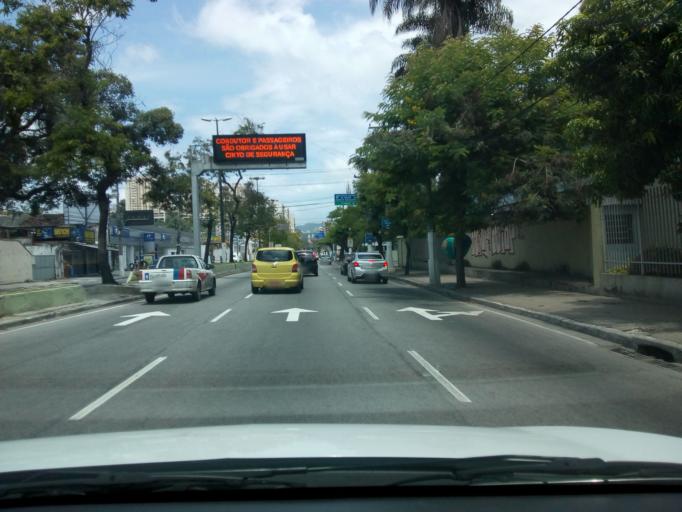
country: BR
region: Rio de Janeiro
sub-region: Niteroi
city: Niteroi
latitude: -22.8863
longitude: -43.1153
